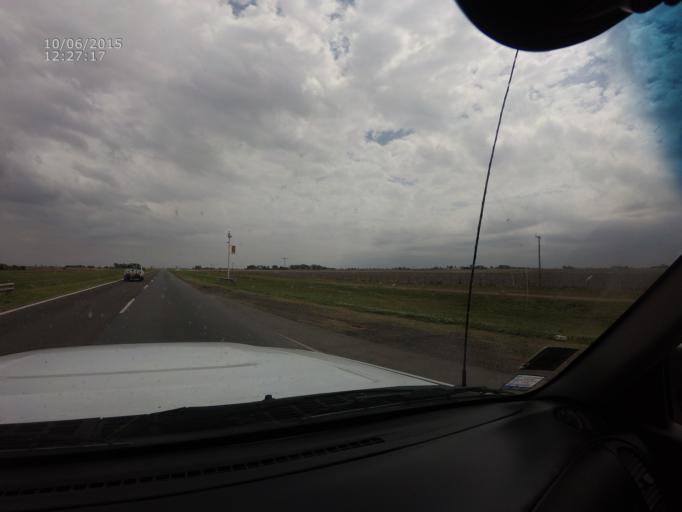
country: AR
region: Santa Fe
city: Carcarana
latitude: -32.9001
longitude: -61.0364
